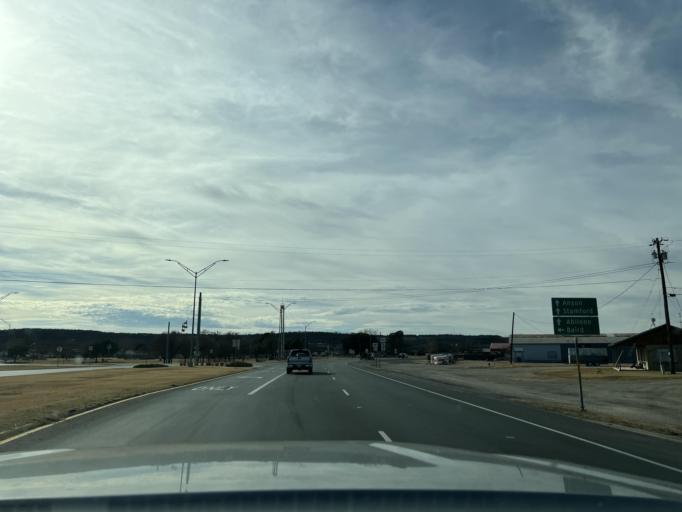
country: US
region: Texas
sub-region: Shackelford County
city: Albany
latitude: 32.7185
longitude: -99.2991
